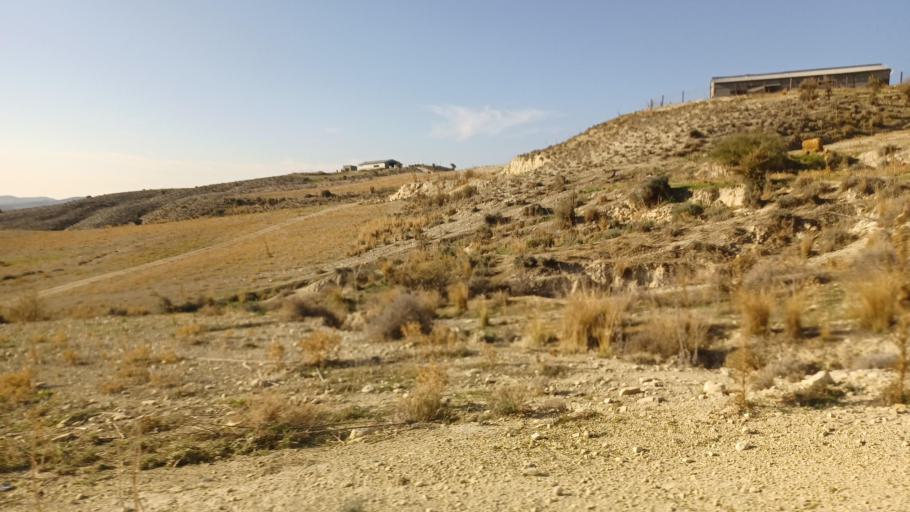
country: CY
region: Larnaka
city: Psevdas
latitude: 34.9483
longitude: 33.5154
